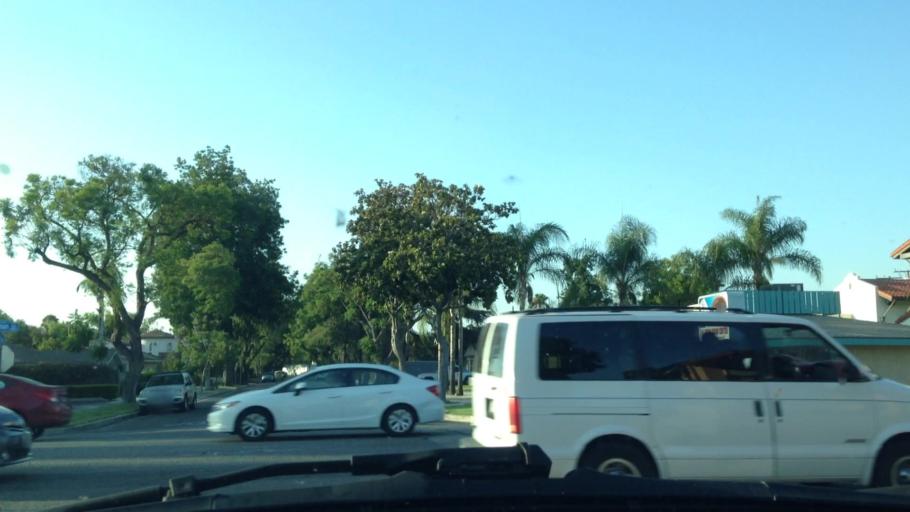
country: US
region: California
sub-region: Orange County
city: Placentia
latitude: 33.8740
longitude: -117.8961
